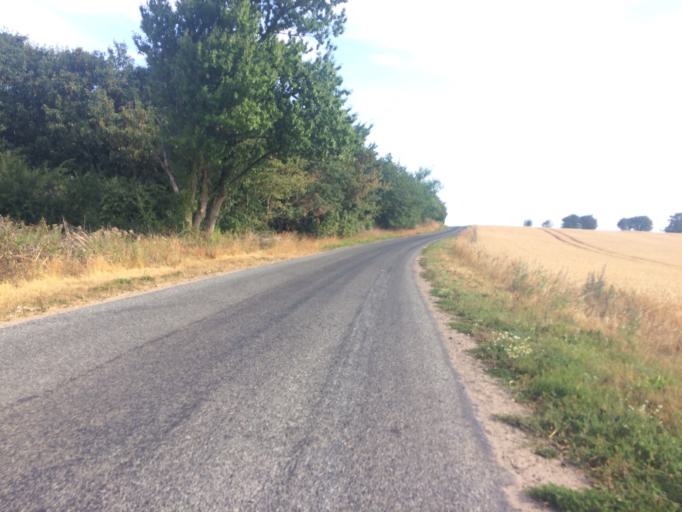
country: DK
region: Central Jutland
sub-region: Holstebro Kommune
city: Vinderup
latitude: 56.6011
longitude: 8.7599
